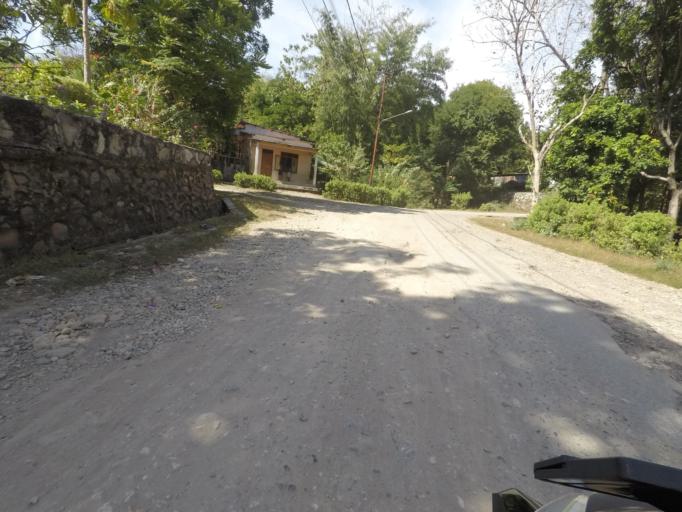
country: TL
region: Bobonaro
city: Maliana
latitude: -8.9935
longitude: 125.2251
